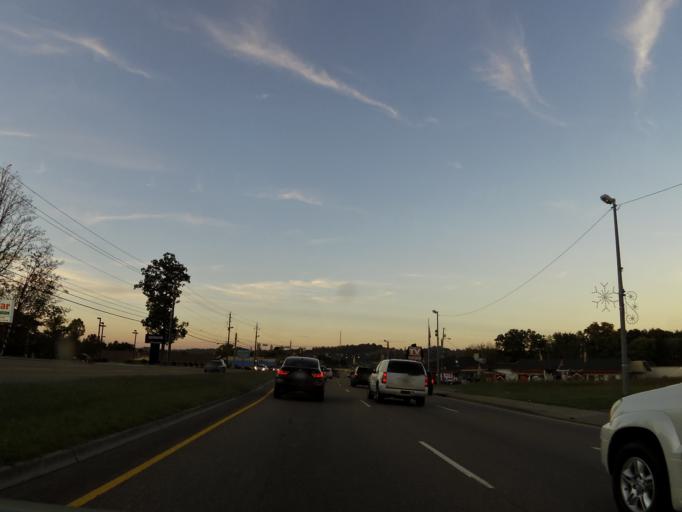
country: US
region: Tennessee
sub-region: Sevier County
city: Sevierville
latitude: 35.8538
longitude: -83.5696
